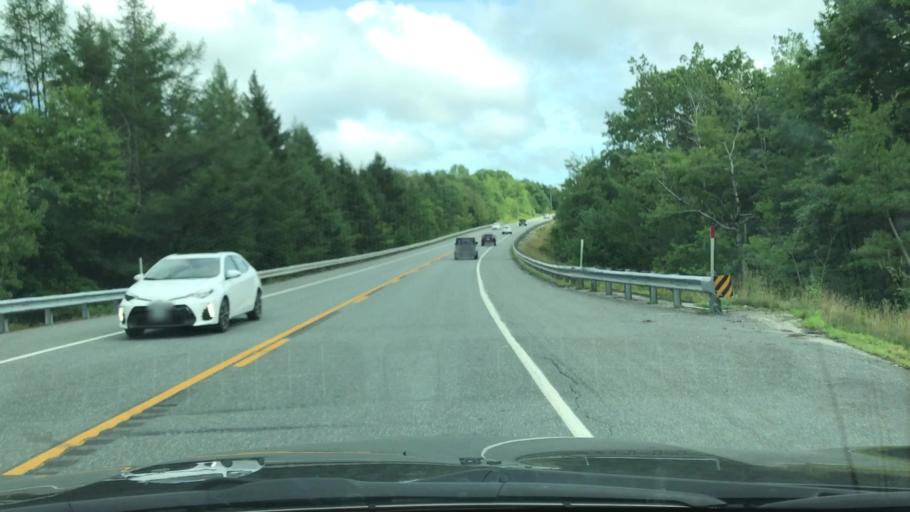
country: US
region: Maine
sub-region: Hancock County
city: Surry
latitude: 44.5564
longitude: -68.5436
